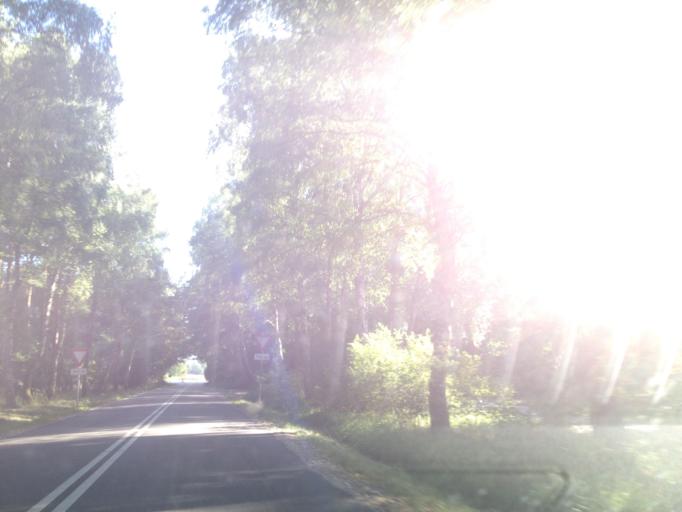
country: DK
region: Capital Region
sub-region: Halsnaes Kommune
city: Frederiksvaerk
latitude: 56.0215
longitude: 12.0790
